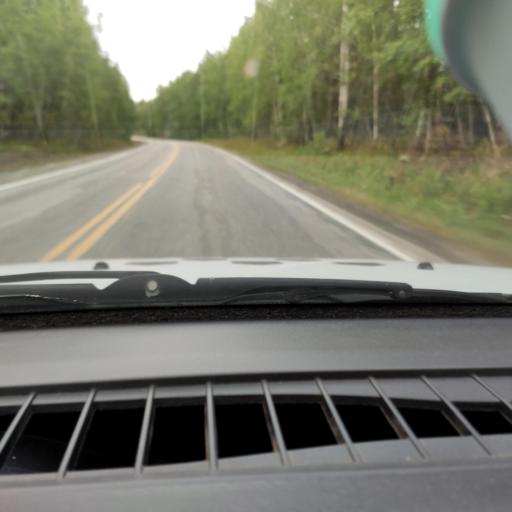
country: RU
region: Chelyabinsk
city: Ozersk
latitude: 55.8093
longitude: 60.6321
